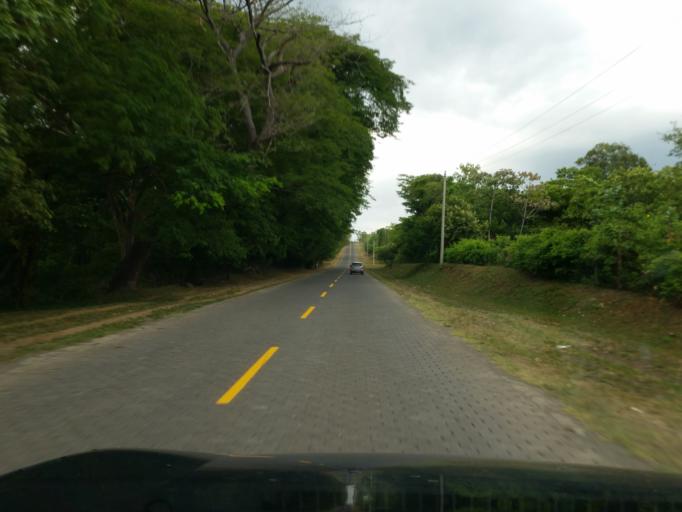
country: NI
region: Managua
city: San Rafael del Sur
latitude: 11.8871
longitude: -86.5142
